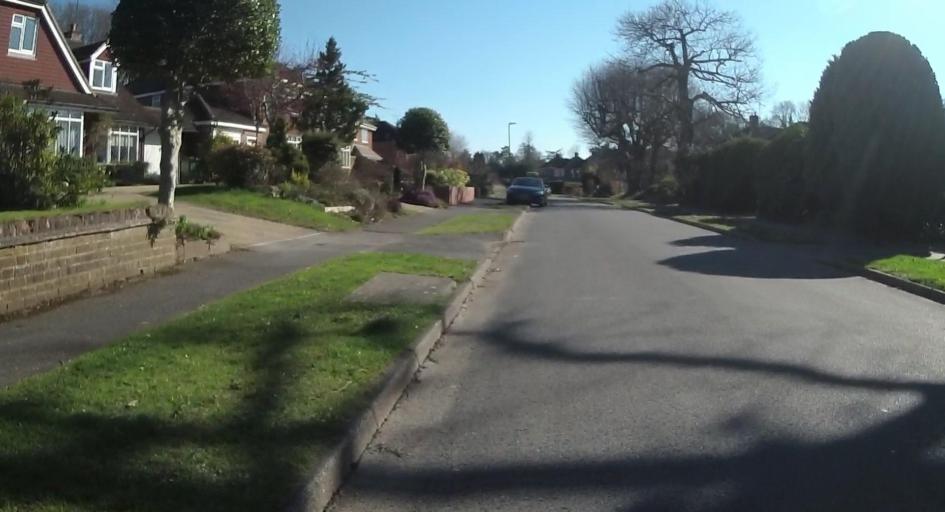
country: GB
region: England
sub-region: Royal Borough of Windsor and Maidenhead
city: Ascot
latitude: 51.4020
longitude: -0.6650
